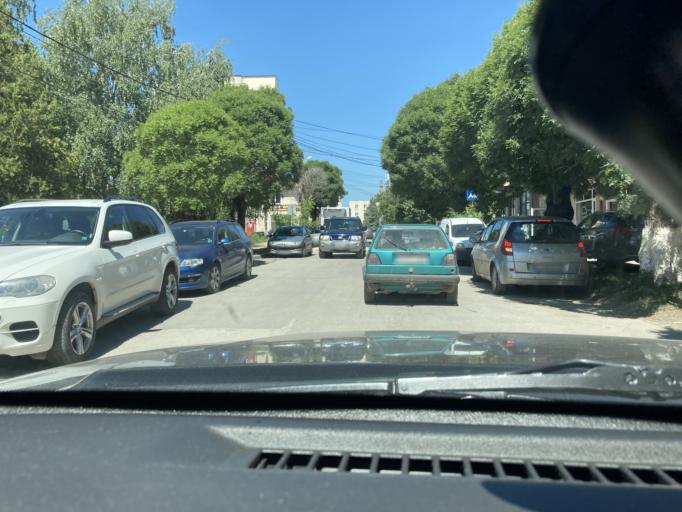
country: BG
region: Sofiya
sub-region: Obshtina Slivnitsa
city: Slivnitsa
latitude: 42.8515
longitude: 23.0403
